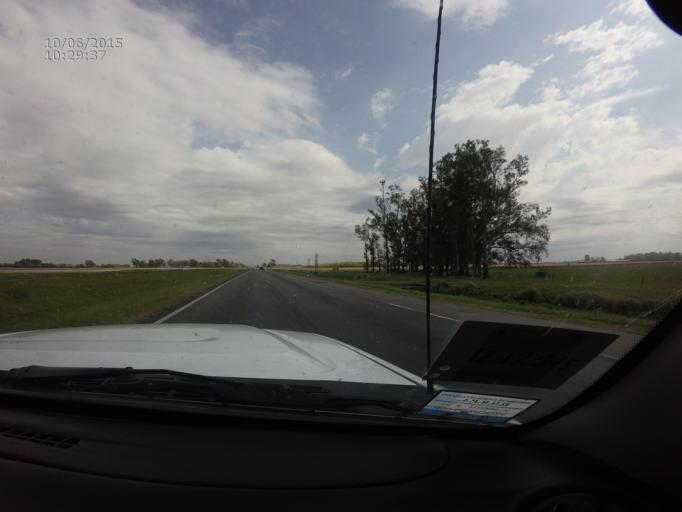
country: AR
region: Buenos Aires
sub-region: Partido de Ramallo
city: Ramallo
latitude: -33.6425
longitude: -59.9796
